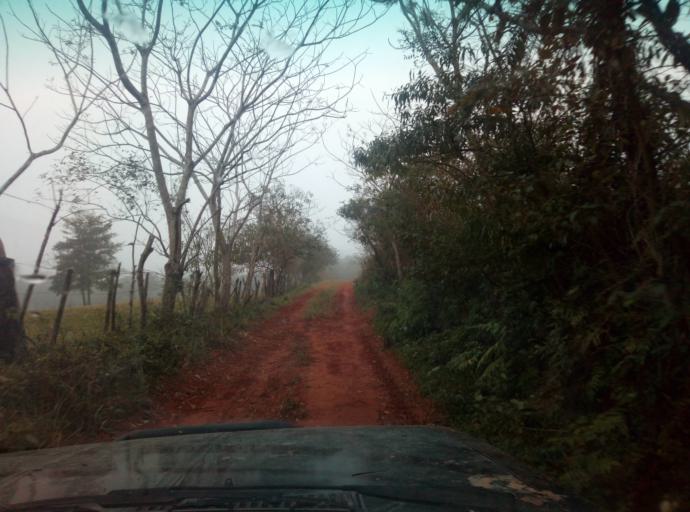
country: PY
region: Caaguazu
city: Doctor Cecilio Baez
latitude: -25.1509
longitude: -56.2548
